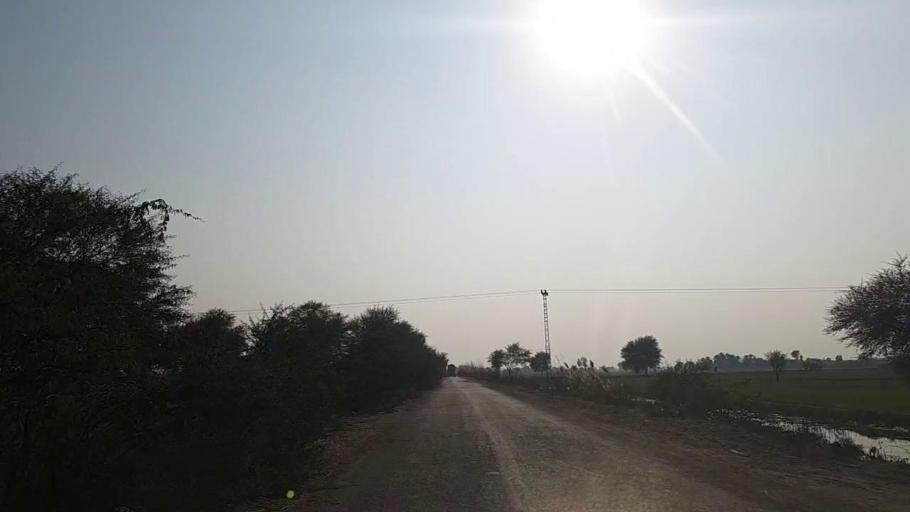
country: PK
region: Sindh
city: Jam Sahib
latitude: 26.2799
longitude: 68.6185
